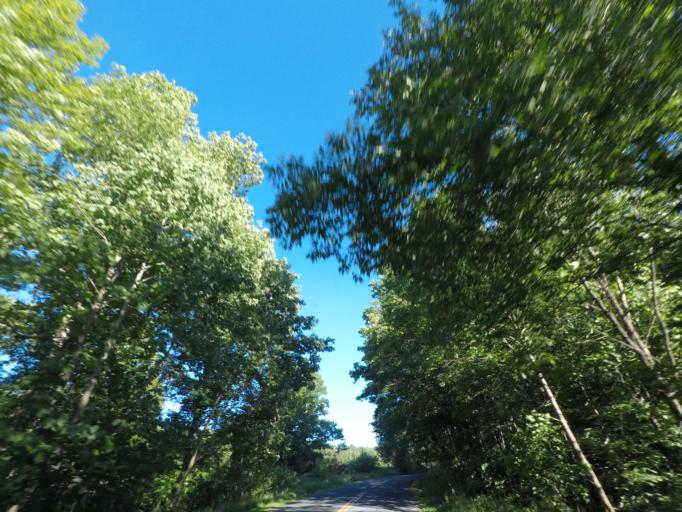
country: US
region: New York
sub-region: Rensselaer County
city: Averill Park
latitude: 42.5748
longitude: -73.5329
